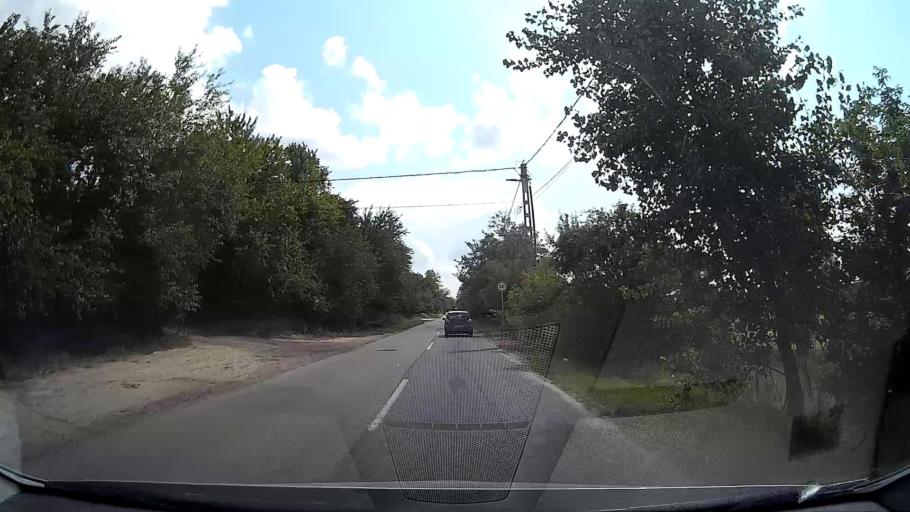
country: HU
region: Pest
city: Leanyfalu
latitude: 47.7158
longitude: 19.1050
